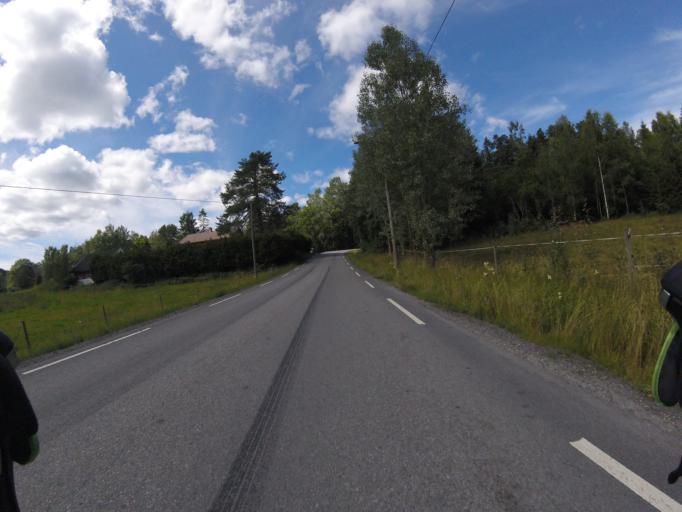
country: NO
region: Akershus
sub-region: Lorenskog
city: Kjenn
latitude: 59.8963
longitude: 10.9703
